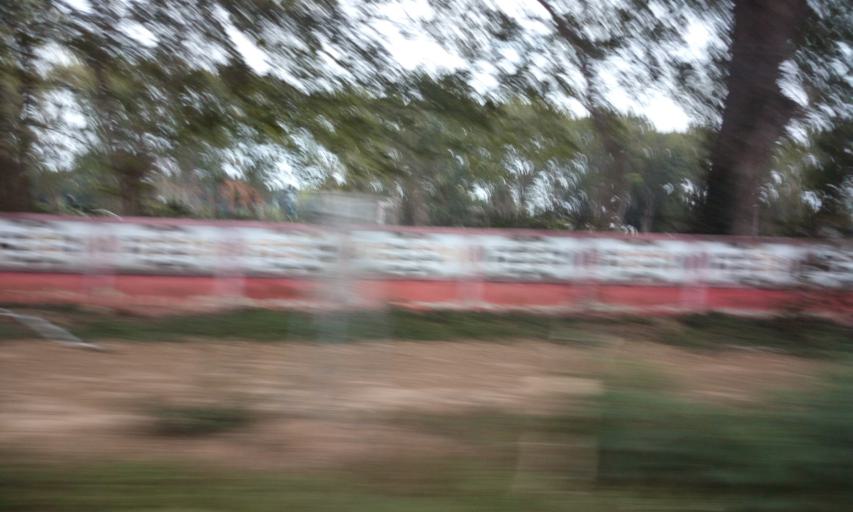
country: TH
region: Phayao
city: Chiang Kham
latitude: 19.5157
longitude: 100.3140
